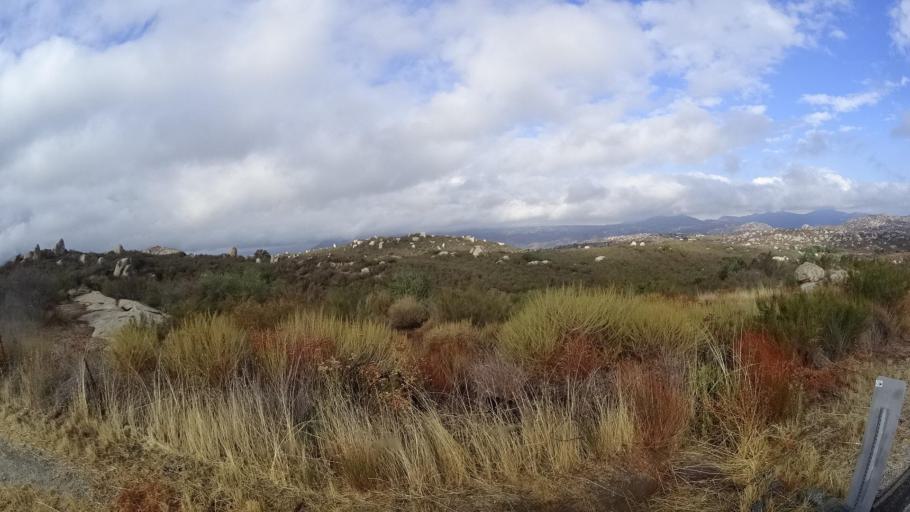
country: MX
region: Baja California
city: Tecate
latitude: 32.6406
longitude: -116.6375
